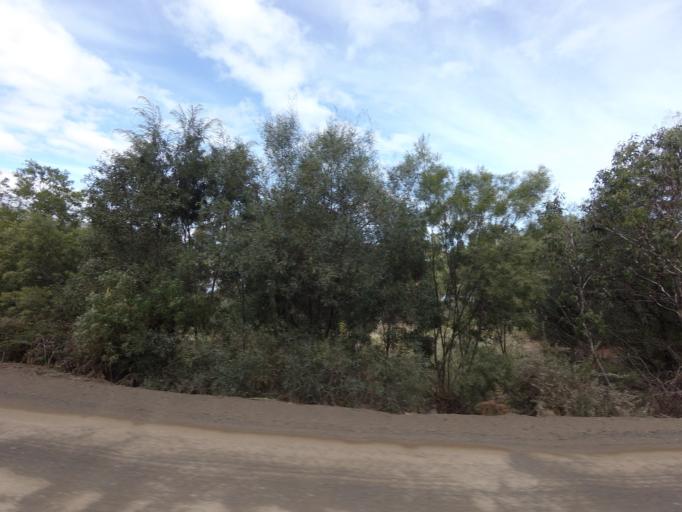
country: AU
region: Tasmania
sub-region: Clarence
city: Sandford
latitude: -43.0937
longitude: 147.7245
